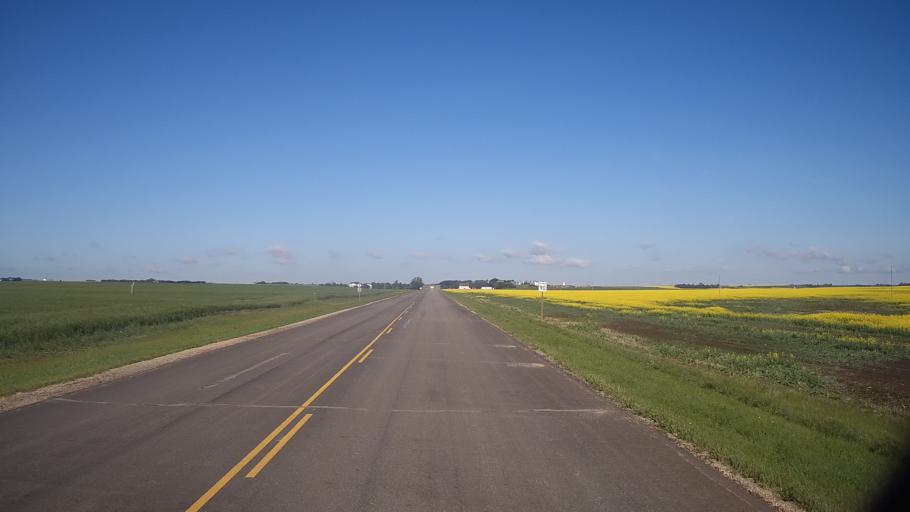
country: CA
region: Saskatchewan
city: Watrous
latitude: 51.6782
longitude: -105.3866
